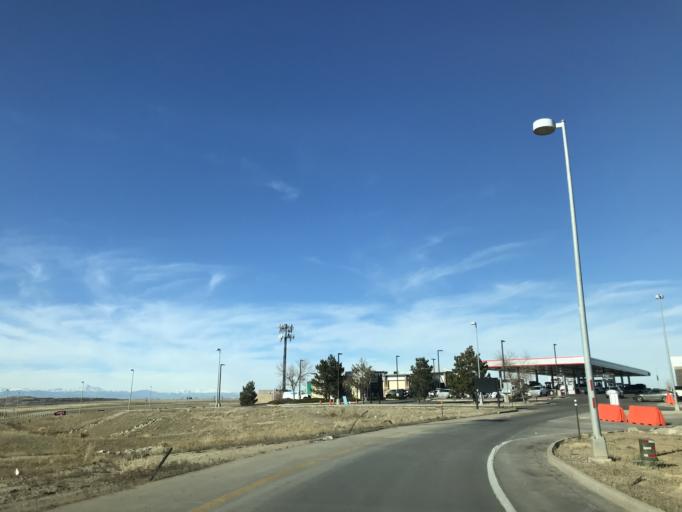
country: US
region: Colorado
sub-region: Adams County
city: Aurora
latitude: 39.8350
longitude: -104.7198
